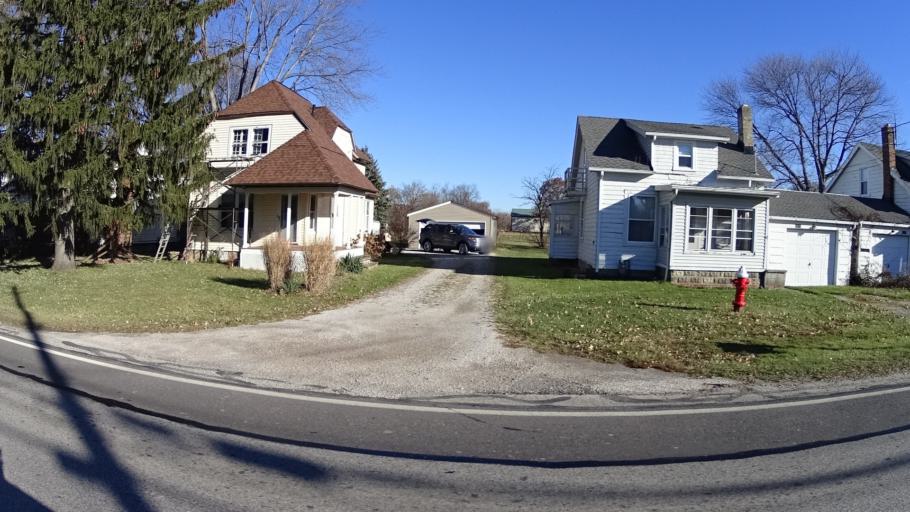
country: US
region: Ohio
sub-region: Lorain County
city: Avon
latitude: 41.4364
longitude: -82.0188
